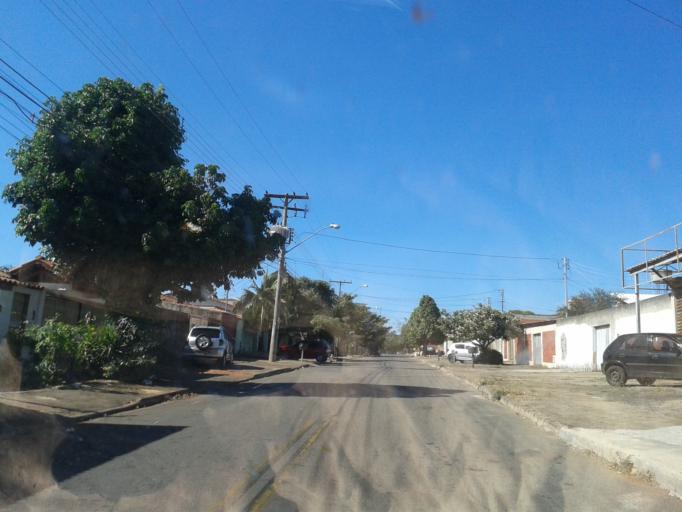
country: BR
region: Goias
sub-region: Goiania
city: Goiania
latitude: -16.7339
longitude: -49.3251
